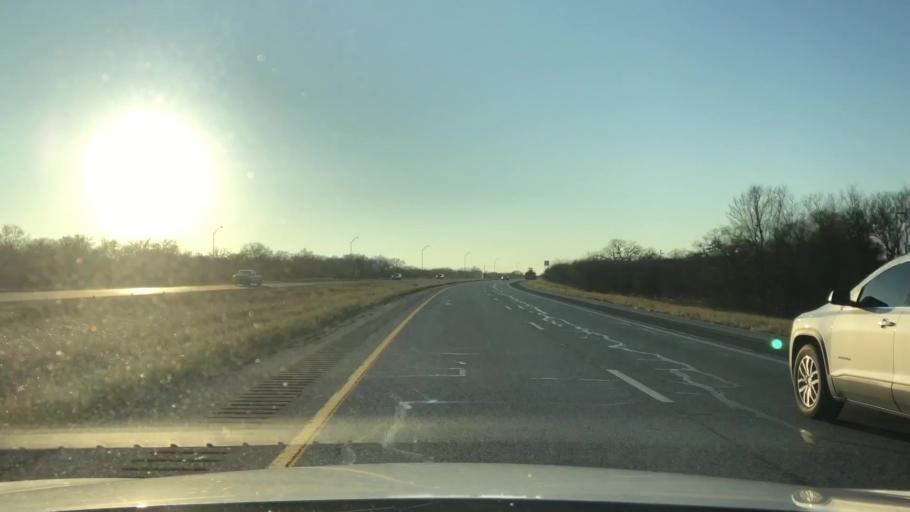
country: US
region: Texas
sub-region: Guadalupe County
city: Seguin
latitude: 29.6155
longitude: -97.8038
